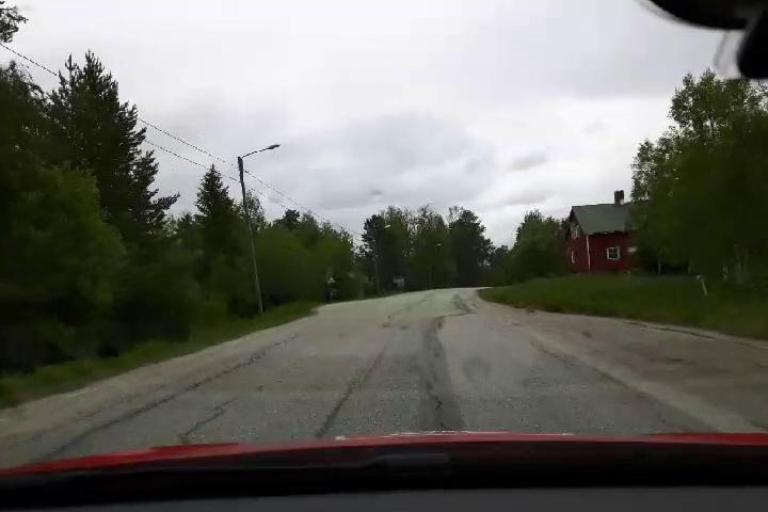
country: SE
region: Jaemtland
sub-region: Bergs Kommun
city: Hoverberg
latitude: 62.7381
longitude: 14.4230
